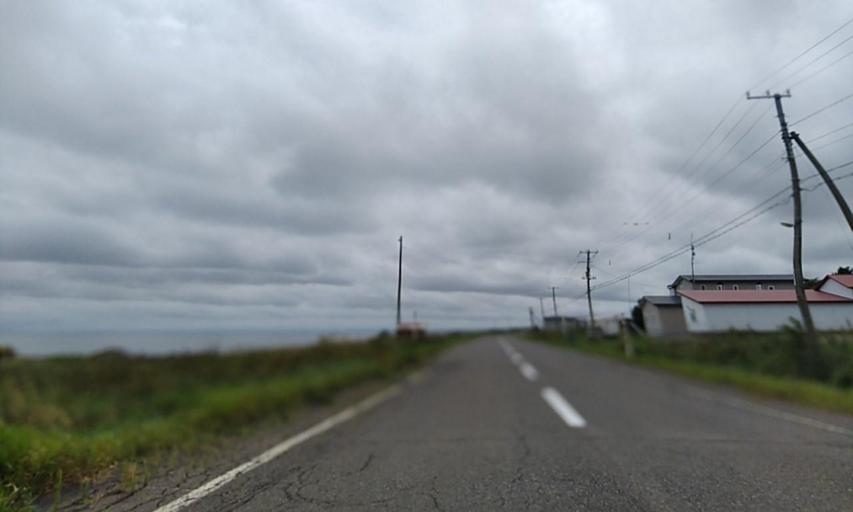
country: JP
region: Hokkaido
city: Shibetsu
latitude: 43.4489
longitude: 145.2613
